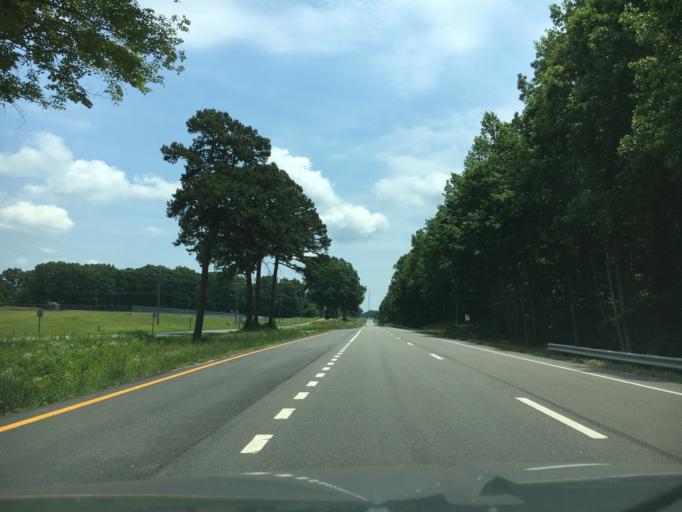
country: US
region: Virginia
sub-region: Buckingham County
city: Buckingham
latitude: 37.5399
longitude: -78.5109
